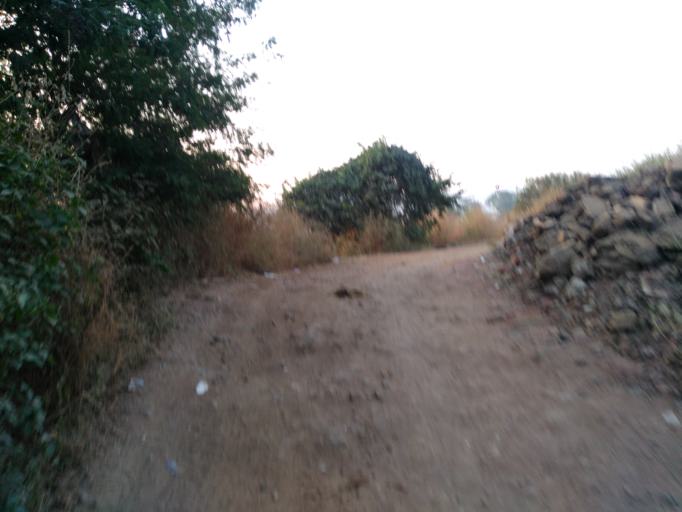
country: IN
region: Maharashtra
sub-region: Pune Division
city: Pune
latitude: 18.4548
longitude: 73.8949
